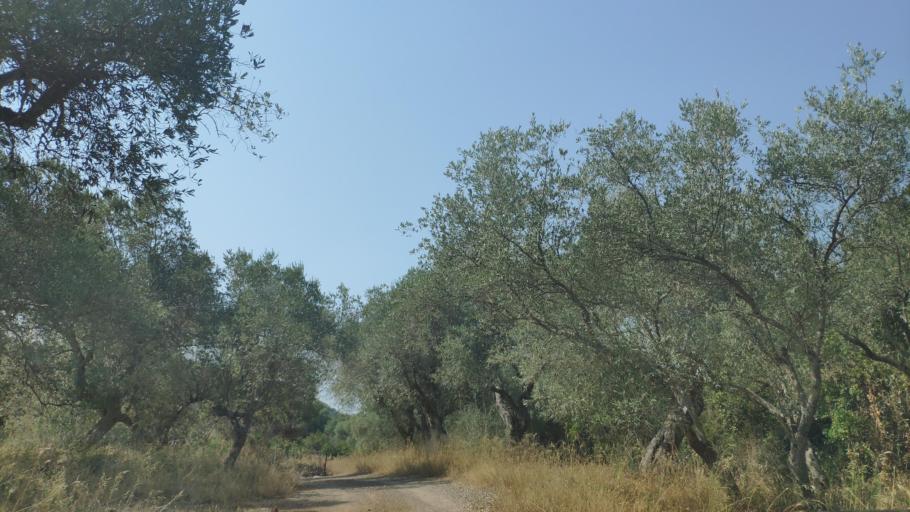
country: GR
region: West Greece
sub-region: Nomos Aitolias kai Akarnanias
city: Fitiai
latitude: 38.7260
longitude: 21.1885
